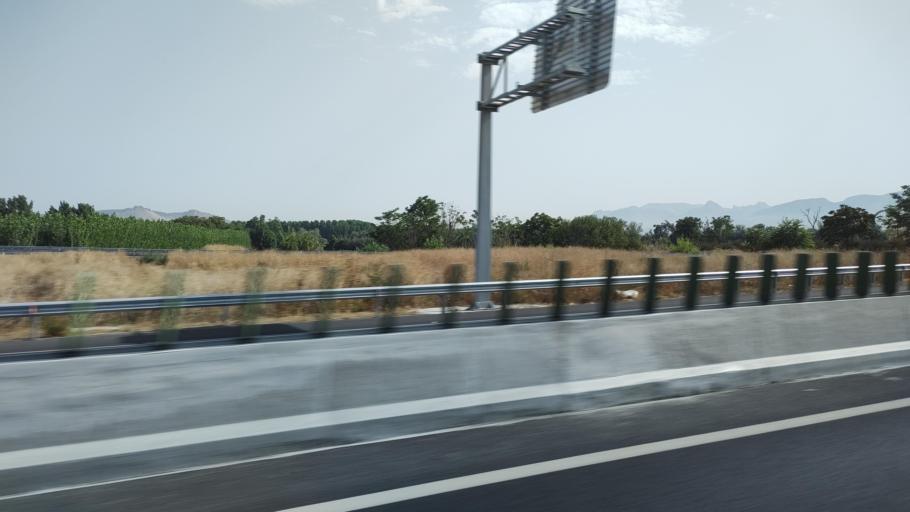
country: ES
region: Andalusia
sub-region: Provincia de Granada
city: Atarfe
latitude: 37.1924
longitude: -3.6918
